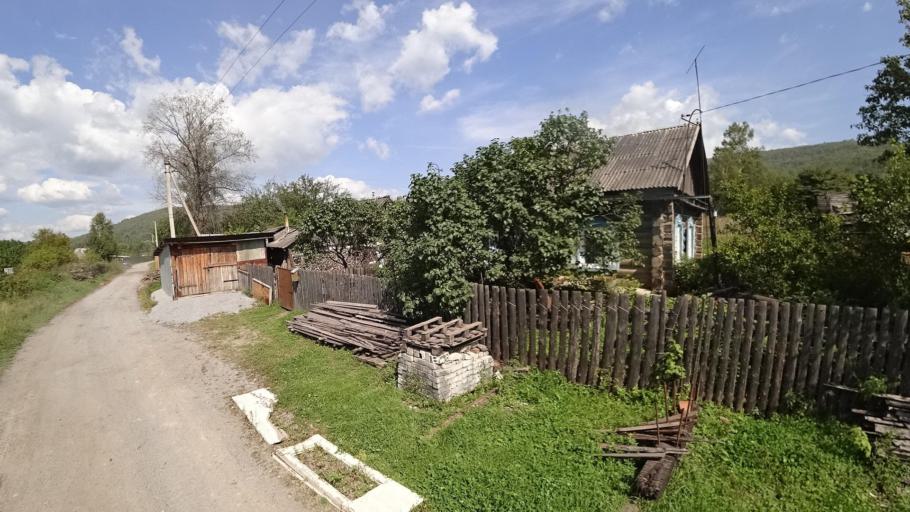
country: RU
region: Jewish Autonomous Oblast
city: Londoko
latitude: 49.0240
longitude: 131.9328
